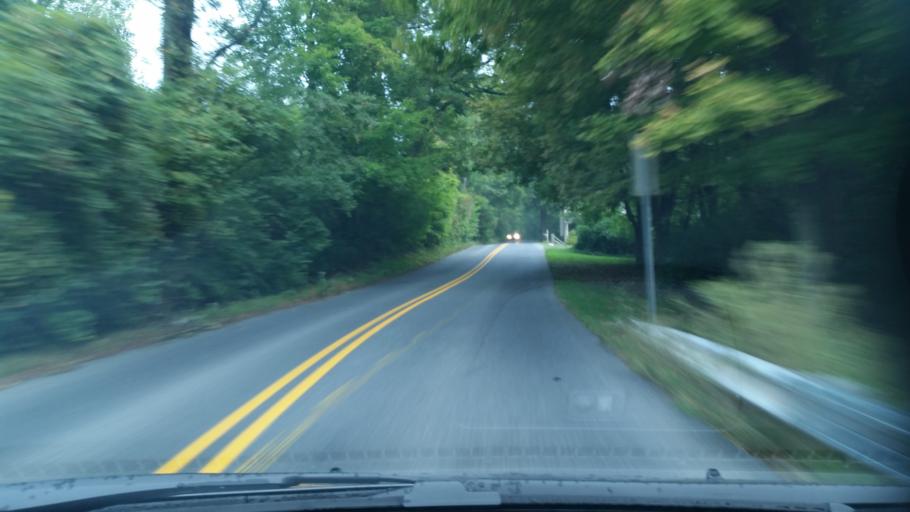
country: US
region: Pennsylvania
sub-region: Lancaster County
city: Lancaster
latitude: 40.0531
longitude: -76.2790
